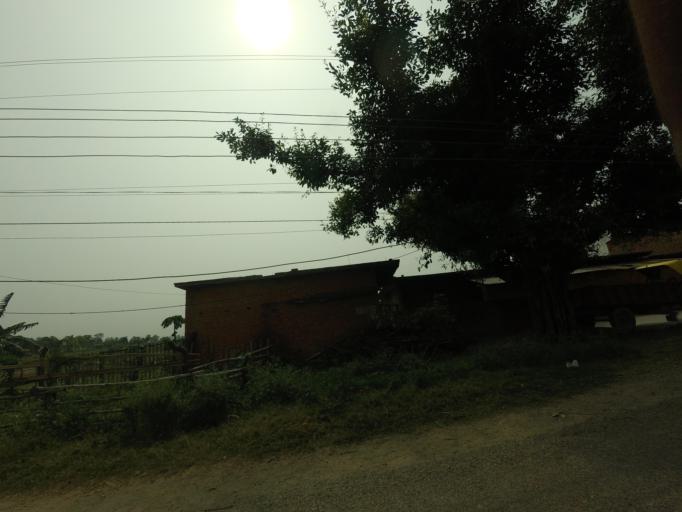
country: IN
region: Uttar Pradesh
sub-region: Maharajganj
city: Nautanwa
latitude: 27.4942
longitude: 83.2844
